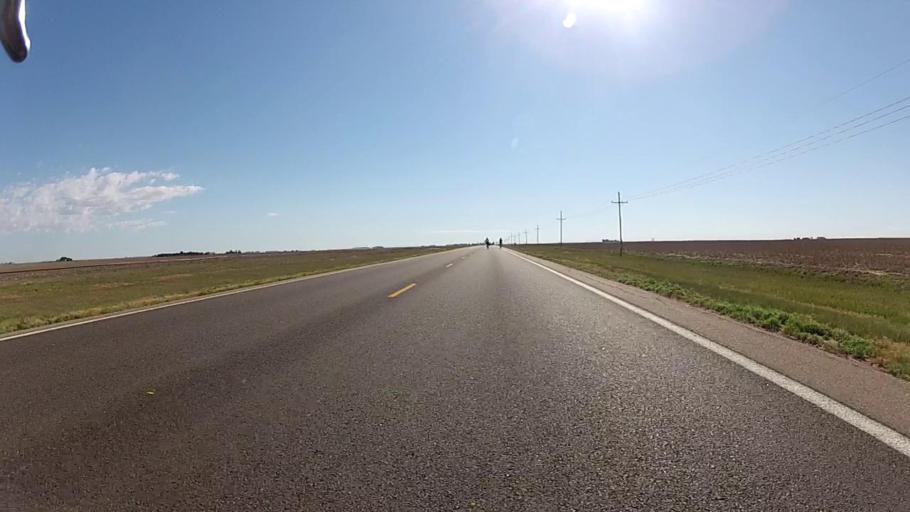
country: US
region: Kansas
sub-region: Gray County
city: Cimarron
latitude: 37.5796
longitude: -100.5128
